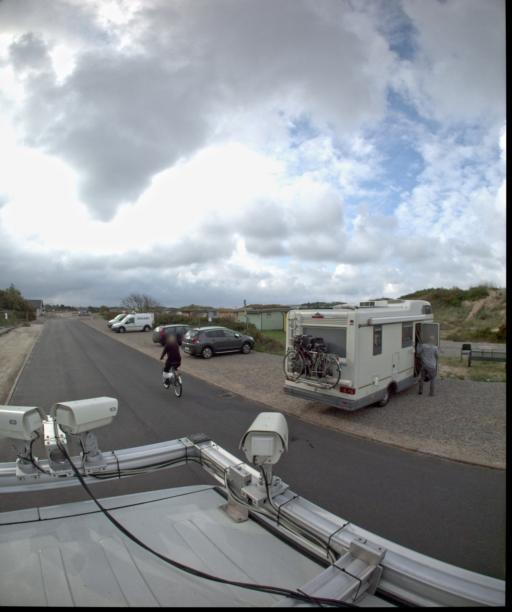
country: SE
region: Halland
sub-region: Falkenbergs Kommun
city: Falkenberg
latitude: 56.8839
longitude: 12.5055
